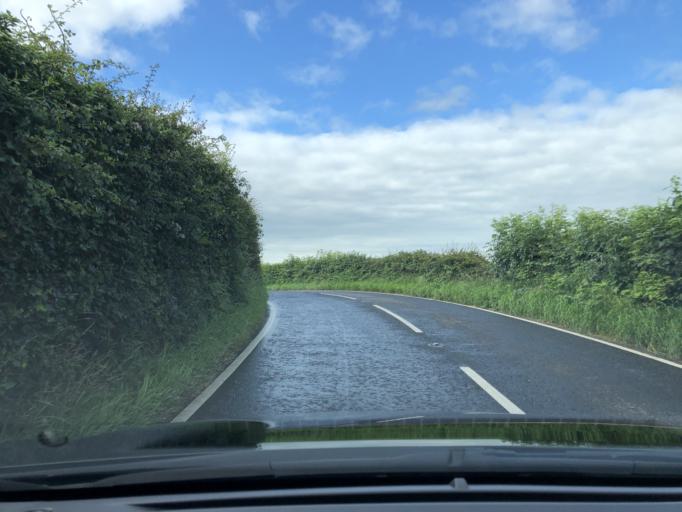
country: GB
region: Northern Ireland
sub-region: Down District
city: Dundrum
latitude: 54.2576
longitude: -5.7796
